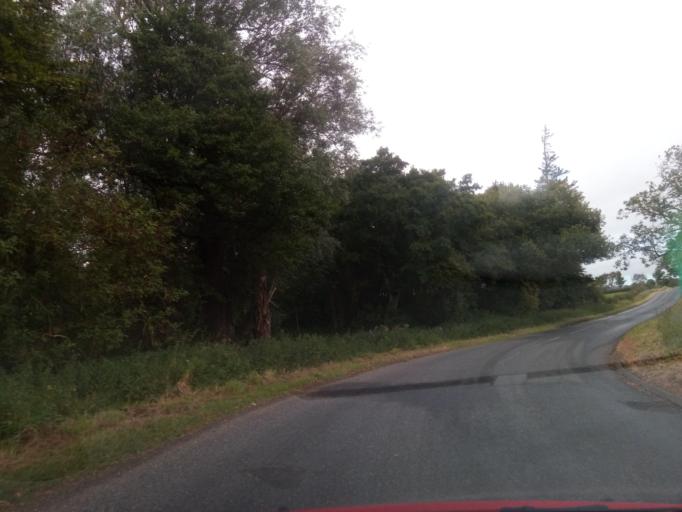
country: GB
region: Scotland
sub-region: The Scottish Borders
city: Duns
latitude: 55.7456
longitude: -2.3200
